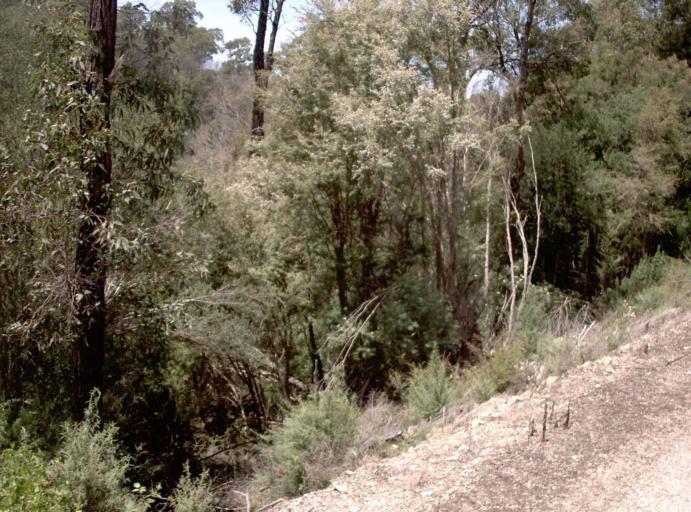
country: AU
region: Victoria
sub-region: East Gippsland
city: Lakes Entrance
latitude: -37.5611
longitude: 147.8868
